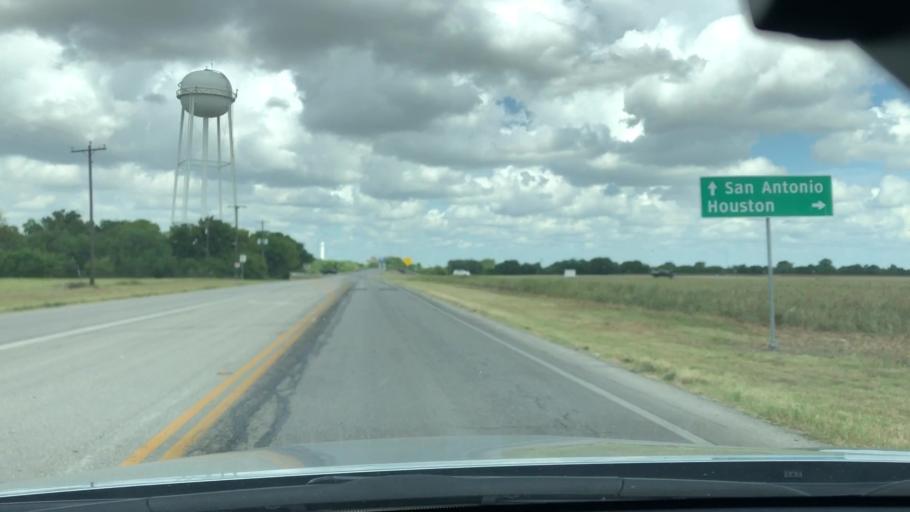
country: US
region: Texas
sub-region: Guadalupe County
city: McQueeney
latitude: 29.5704
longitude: -98.0111
